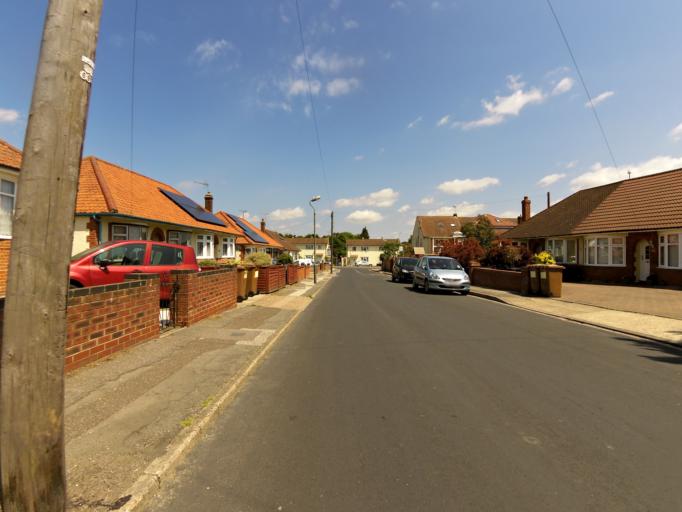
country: GB
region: England
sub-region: Suffolk
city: Bramford
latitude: 52.0712
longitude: 1.1212
